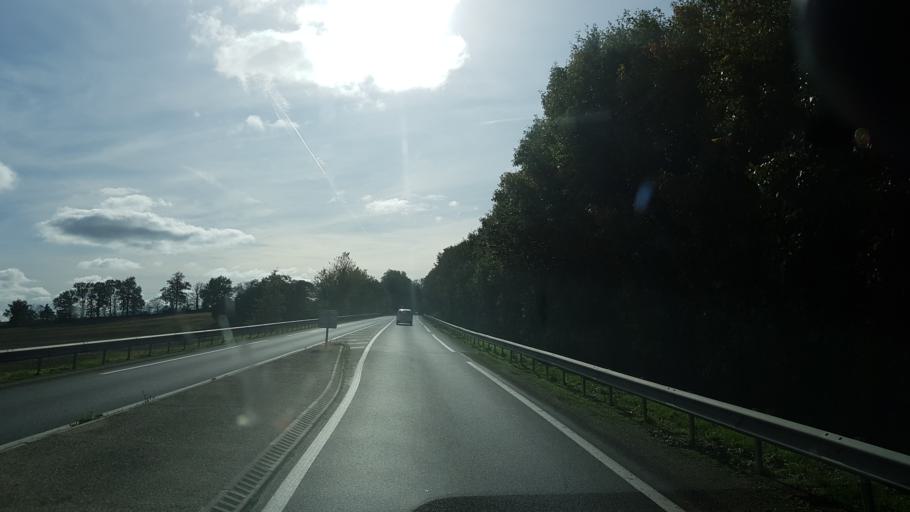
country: FR
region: Poitou-Charentes
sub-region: Departement de la Charente
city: Confolens
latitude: 45.9957
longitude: 0.6302
